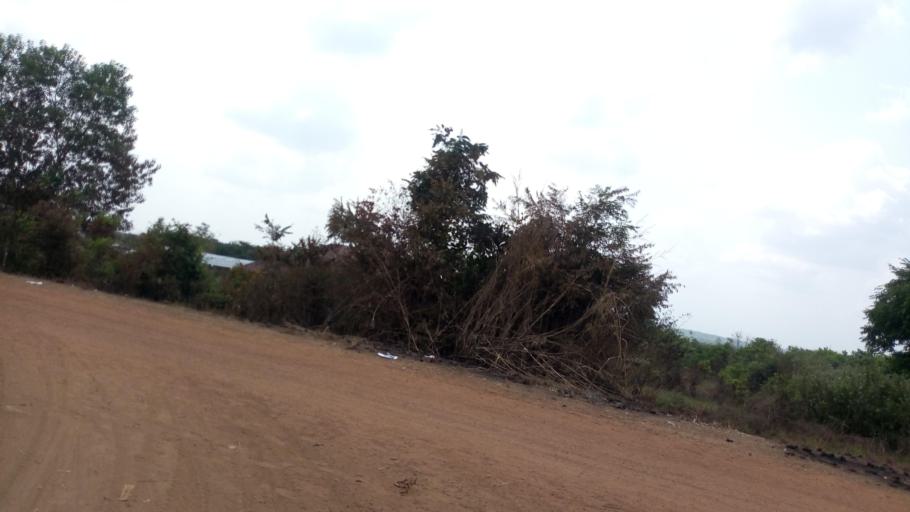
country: SL
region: Southern Province
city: Mogbwemo
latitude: 7.7908
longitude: -12.3068
